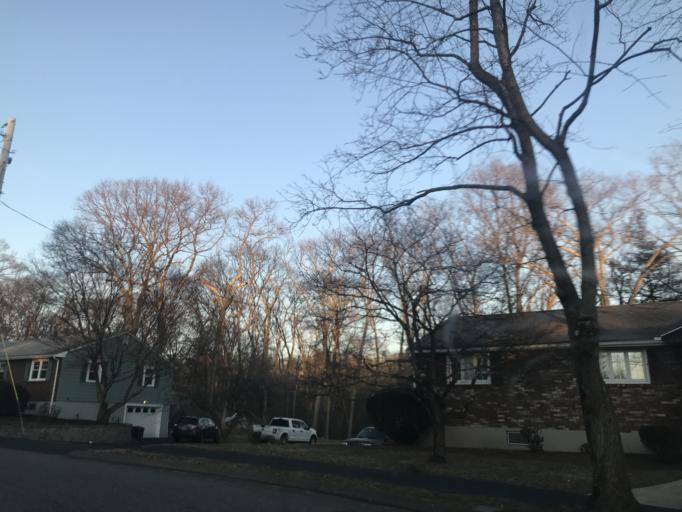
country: US
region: Massachusetts
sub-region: Essex County
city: Saugus
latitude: 42.4770
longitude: -71.0126
